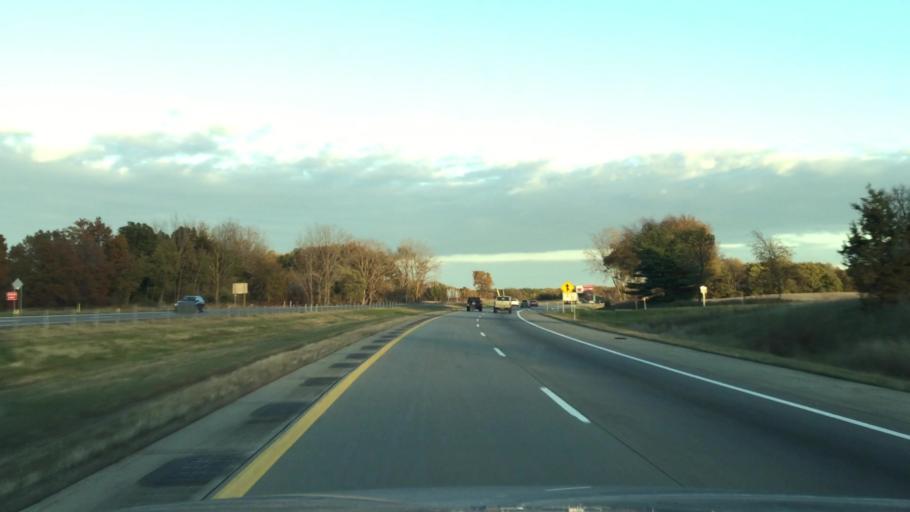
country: US
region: Michigan
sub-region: Calhoun County
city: Albion
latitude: 42.2836
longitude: -84.7998
